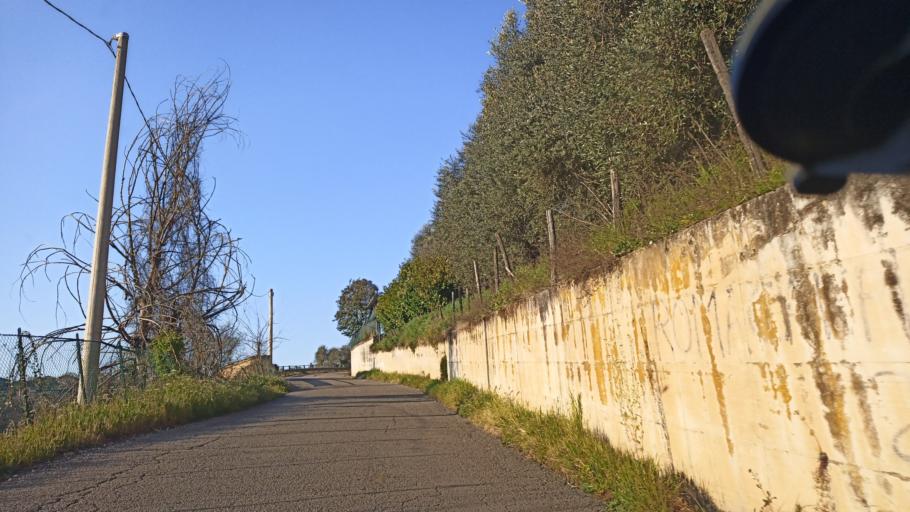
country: IT
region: Latium
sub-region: Provincia di Rieti
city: Poggio Mirteto
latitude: 42.2643
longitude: 12.6800
